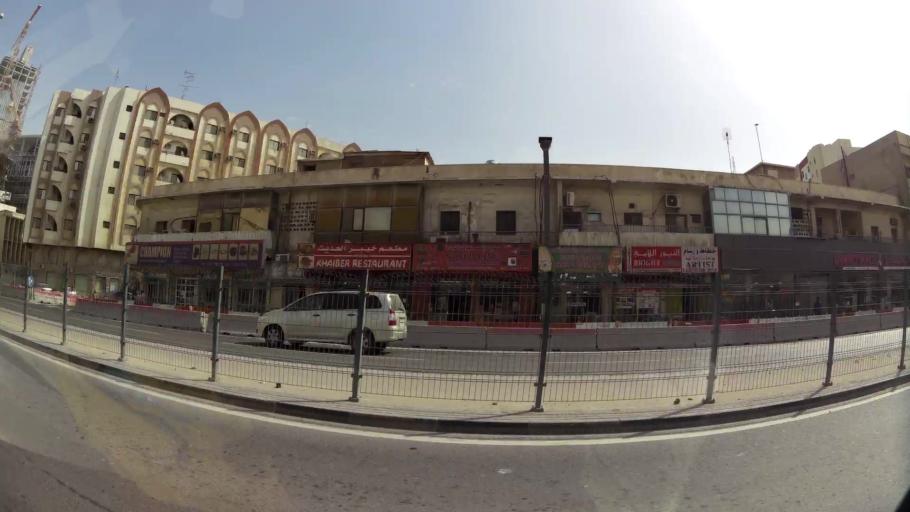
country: QA
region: Baladiyat ad Dawhah
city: Doha
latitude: 25.2828
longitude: 51.5176
